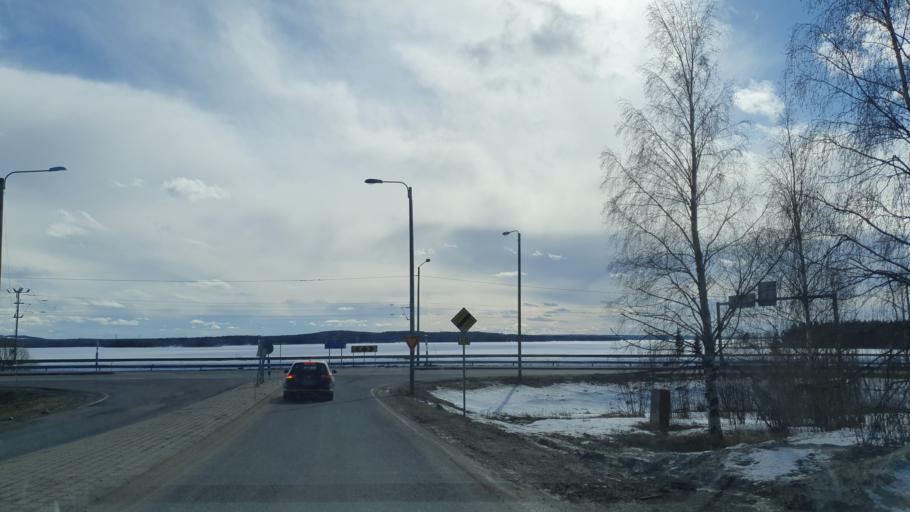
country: FI
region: Kainuu
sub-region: Kajaani
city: Paltamo
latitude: 64.4036
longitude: 27.8381
